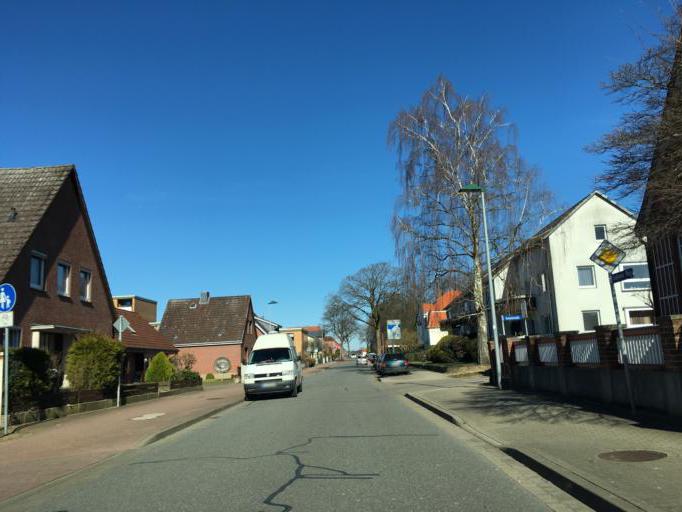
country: DE
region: Schleswig-Holstein
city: Molln
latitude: 53.6222
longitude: 10.6913
